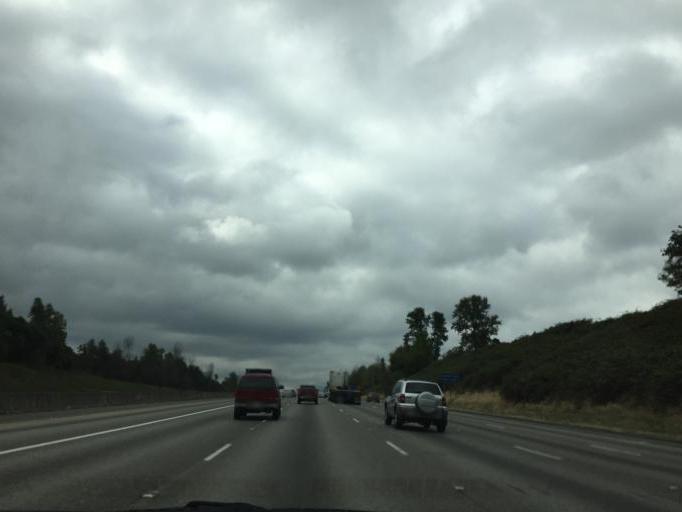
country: US
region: Washington
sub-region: King County
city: SeaTac
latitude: 47.4430
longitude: -122.2685
